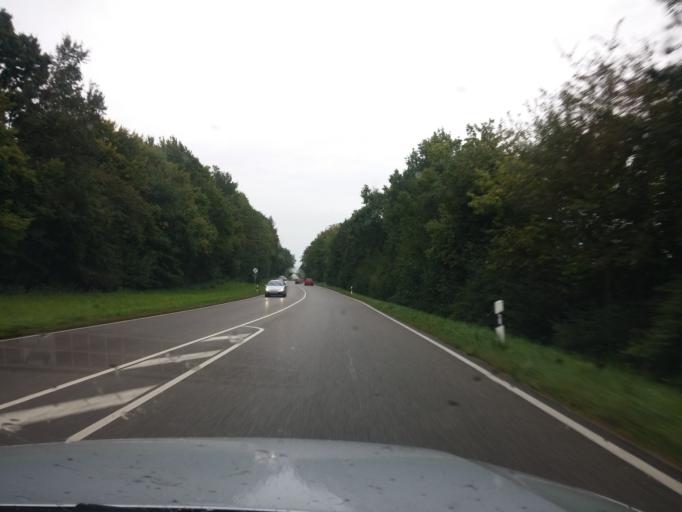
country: DE
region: Bavaria
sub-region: Upper Bavaria
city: Ilmmunster
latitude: 48.4834
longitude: 11.5104
